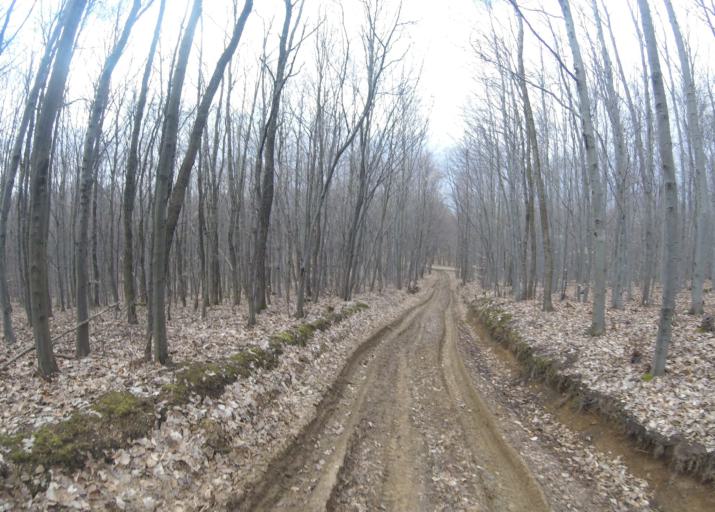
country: HU
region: Heves
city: Belapatfalva
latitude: 48.0289
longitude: 20.3676
